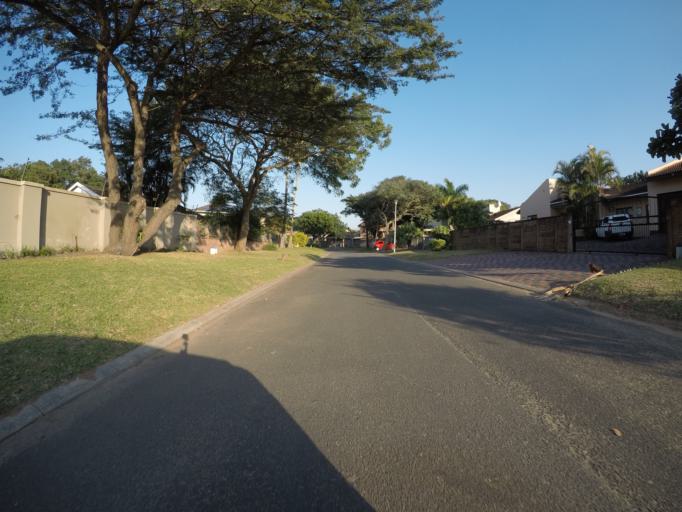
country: ZA
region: KwaZulu-Natal
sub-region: uThungulu District Municipality
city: Richards Bay
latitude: -28.7770
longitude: 32.1144
